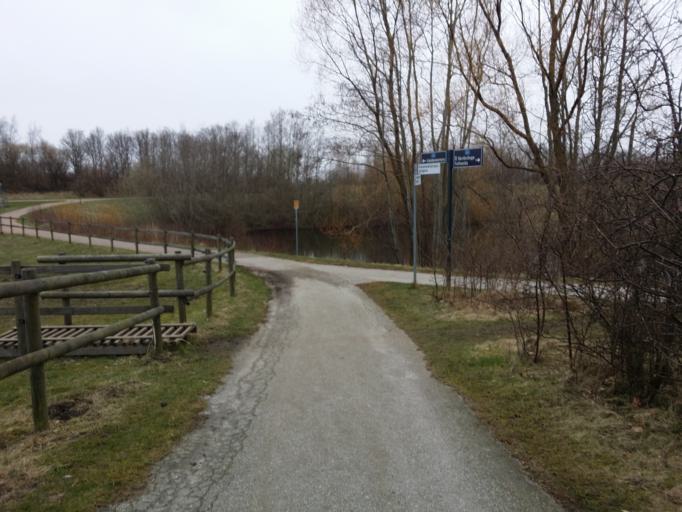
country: SE
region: Skane
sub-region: Burlovs Kommun
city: Arloev
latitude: 55.6063
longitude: 13.0854
